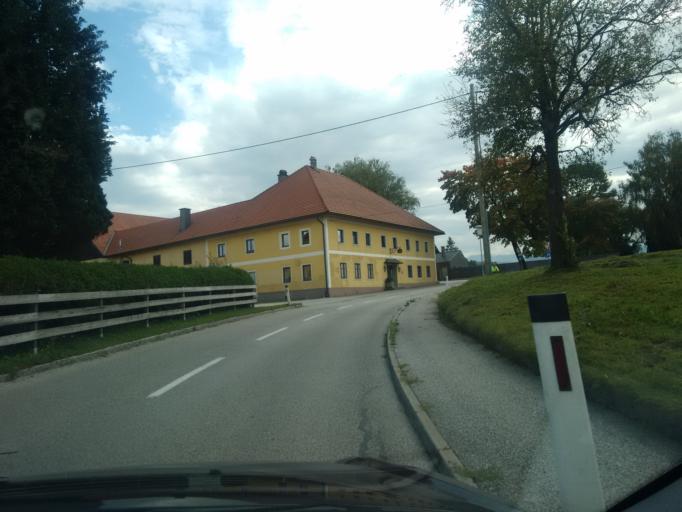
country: AT
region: Upper Austria
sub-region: Politischer Bezirk Vocklabruck
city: Lenzing
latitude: 47.9645
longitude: 13.6319
